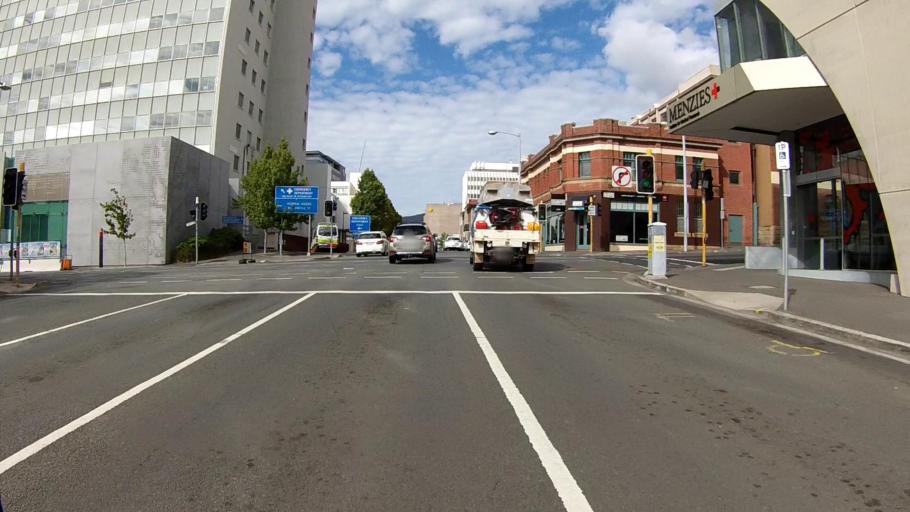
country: AU
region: Tasmania
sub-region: Hobart
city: Hobart
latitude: -42.8789
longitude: 147.3300
